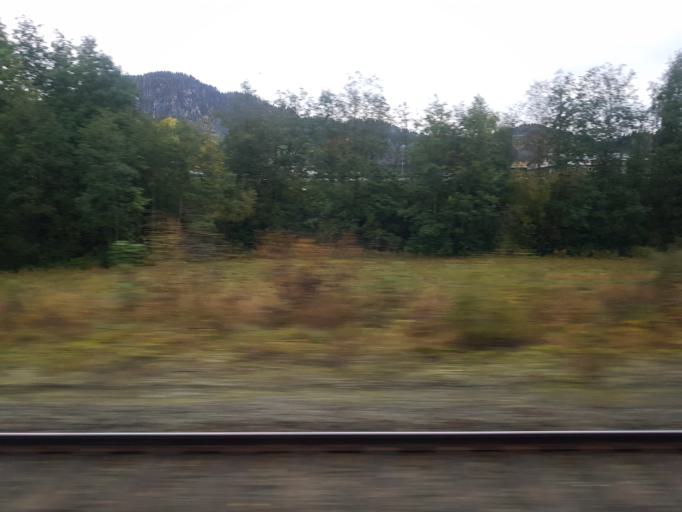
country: NO
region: Sor-Trondelag
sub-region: Melhus
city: Lundamo
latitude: 63.1337
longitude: 10.2576
